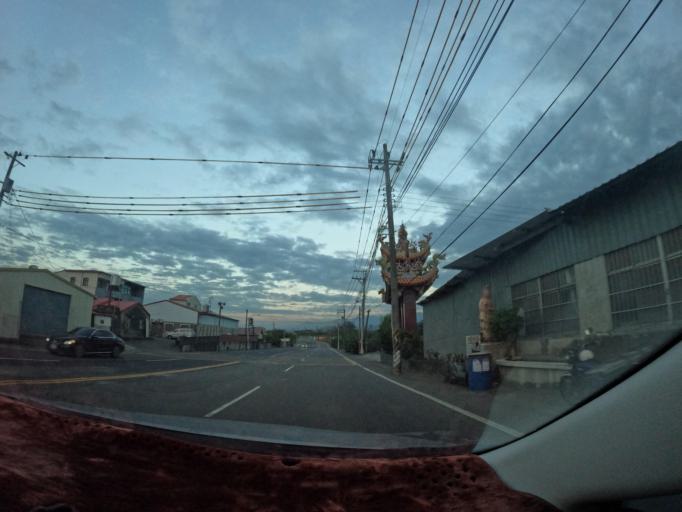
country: TW
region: Taiwan
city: Yujing
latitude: 23.0984
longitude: 120.4437
